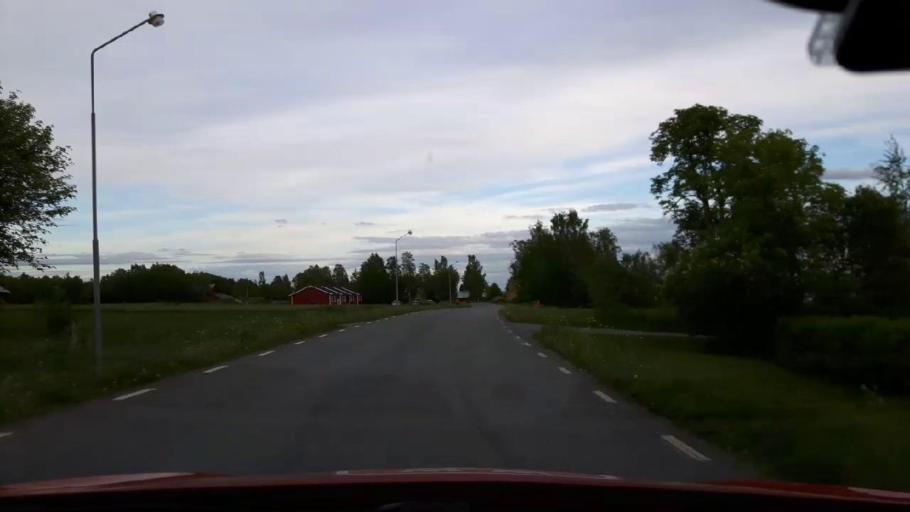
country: SE
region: Jaemtland
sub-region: OEstersunds Kommun
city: Ostersund
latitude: 63.0445
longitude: 14.4556
